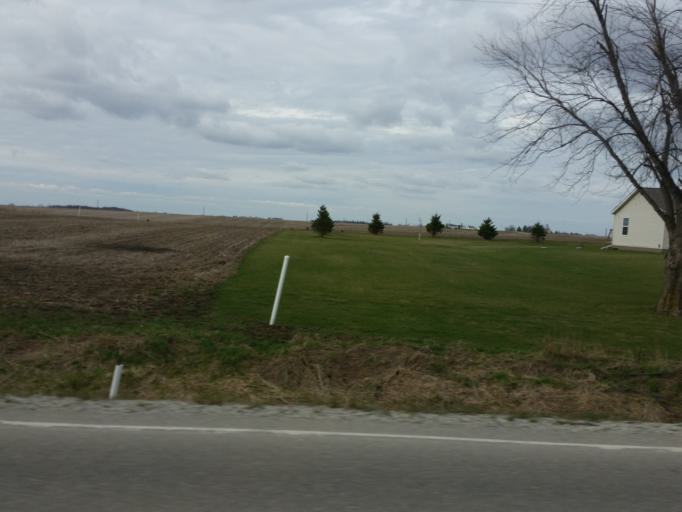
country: US
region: Iowa
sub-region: Black Hawk County
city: Elk Run Heights
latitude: 42.5703
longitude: -92.2239
